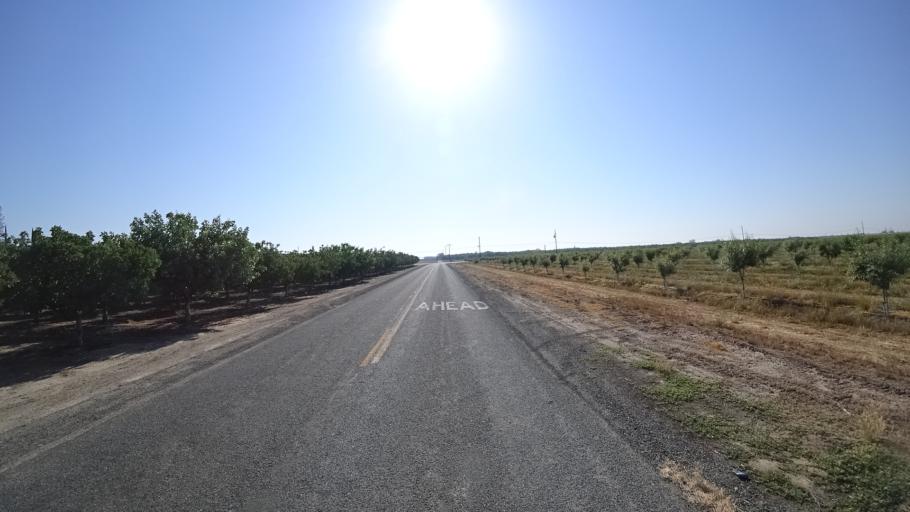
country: US
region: California
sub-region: Kings County
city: Lucerne
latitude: 36.3935
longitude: -119.6753
